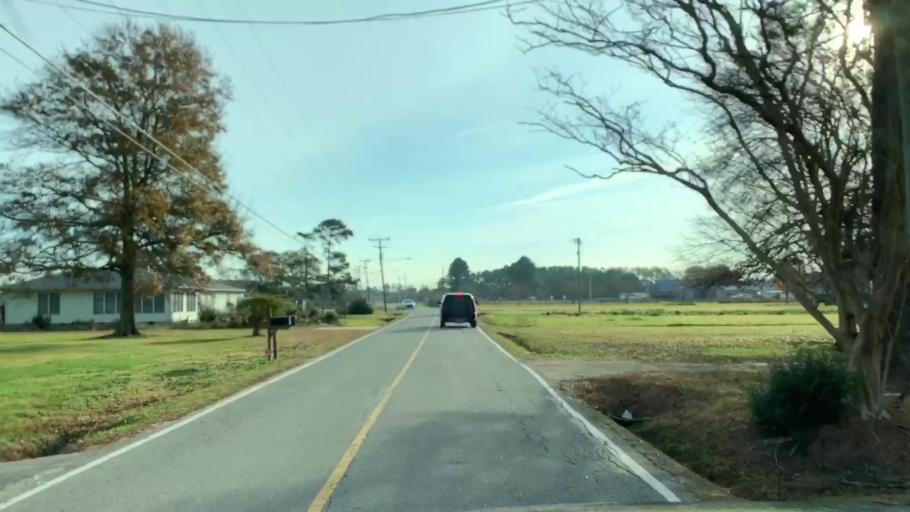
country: US
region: Virginia
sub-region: City of Virginia Beach
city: Virginia Beach
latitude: 36.6906
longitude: -76.0123
